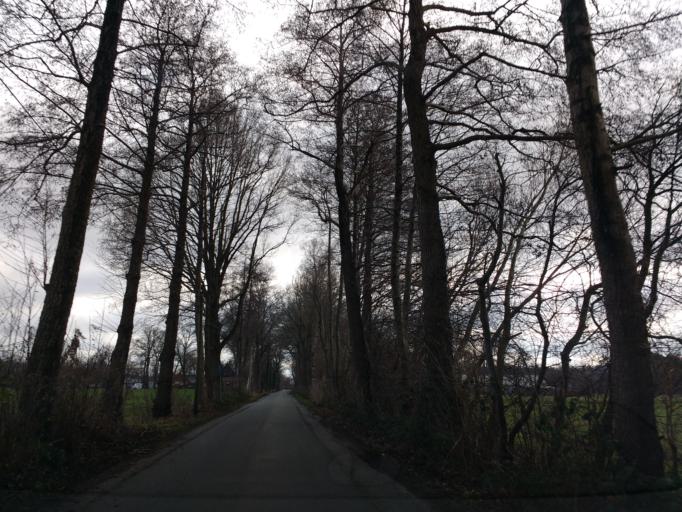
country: DE
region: North Rhine-Westphalia
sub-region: Regierungsbezirk Detmold
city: Hovelhof
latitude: 51.8238
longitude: 8.6912
